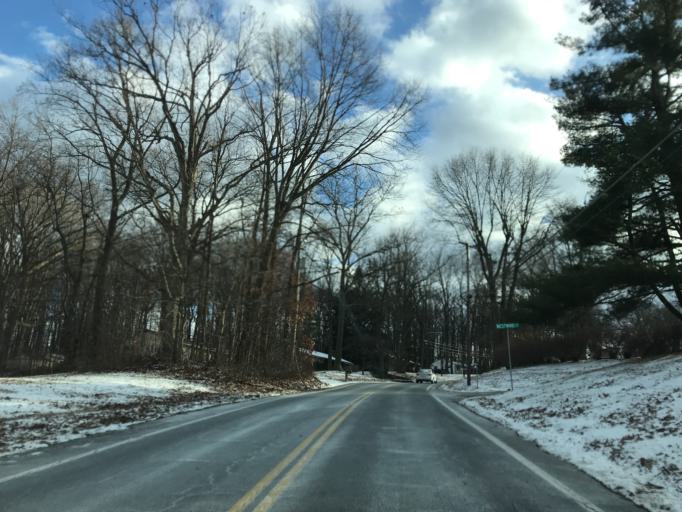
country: US
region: Maryland
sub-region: Harford County
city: Bel Air North
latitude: 39.6505
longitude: -76.3823
